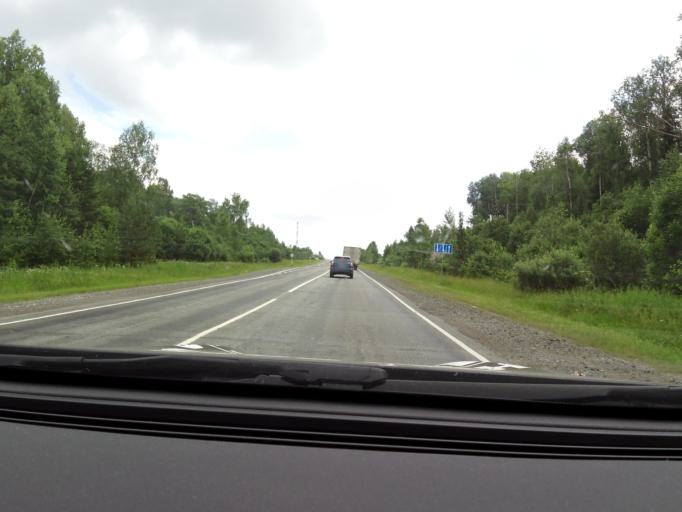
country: RU
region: Sverdlovsk
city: Achit
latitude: 56.8616
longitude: 57.6886
